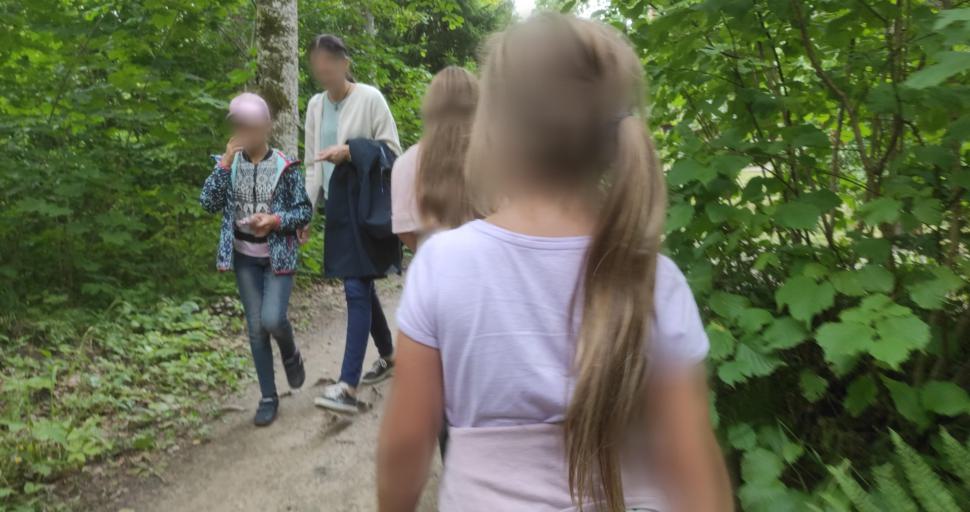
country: LV
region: Kuldigas Rajons
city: Kuldiga
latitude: 57.0069
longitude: 21.9854
